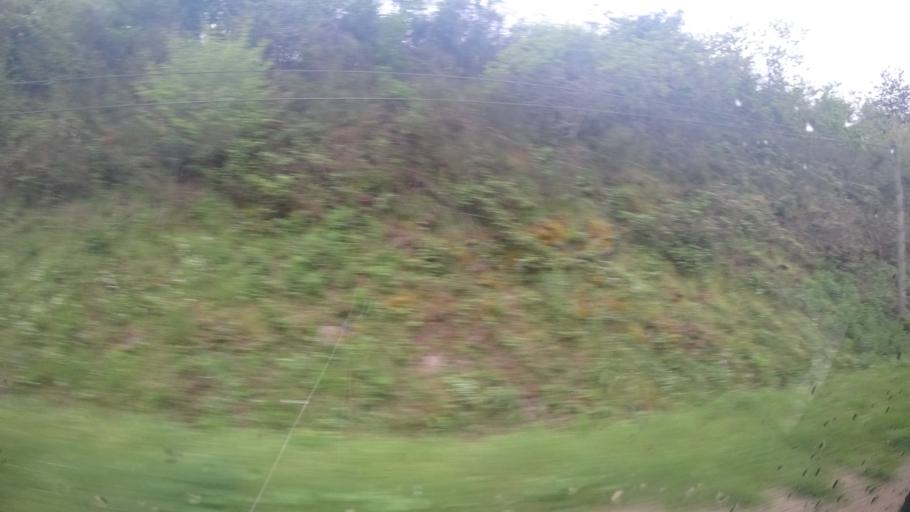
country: FR
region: Midi-Pyrenees
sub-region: Departement de l'Aveyron
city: Salles-Curan
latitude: 44.2697
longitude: 2.8673
